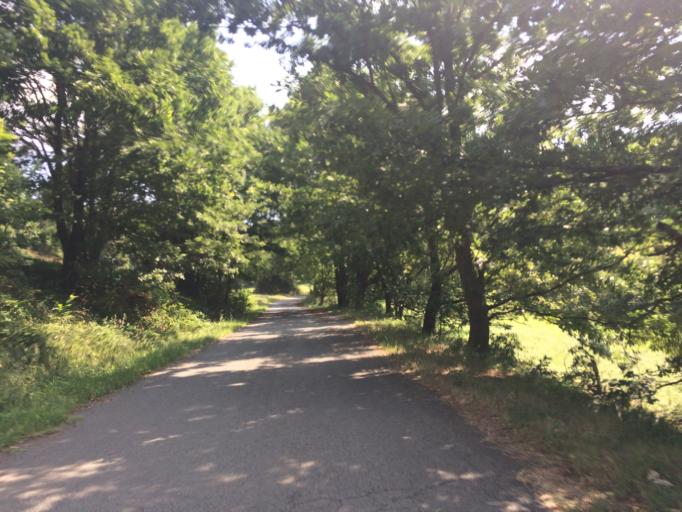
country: IT
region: Piedmont
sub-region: Provincia di Alessandria
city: Pareto
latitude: 44.4993
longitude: 8.3641
